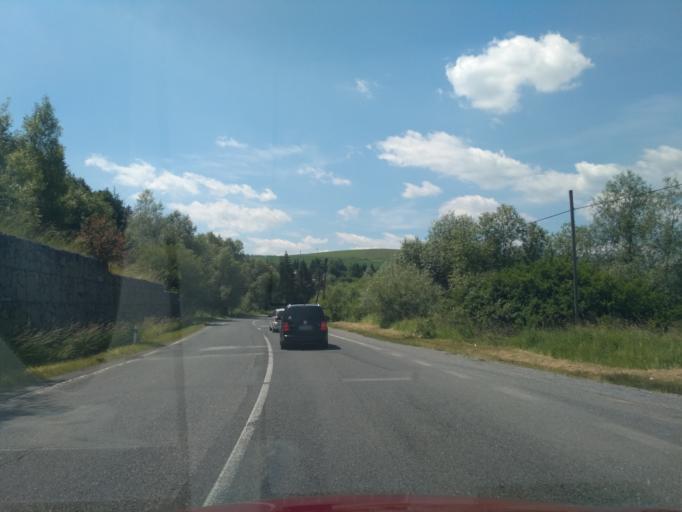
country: PL
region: Lesser Poland Voivodeship
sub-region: Powiat nowosadecki
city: Muszyna
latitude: 49.2574
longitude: 20.8471
